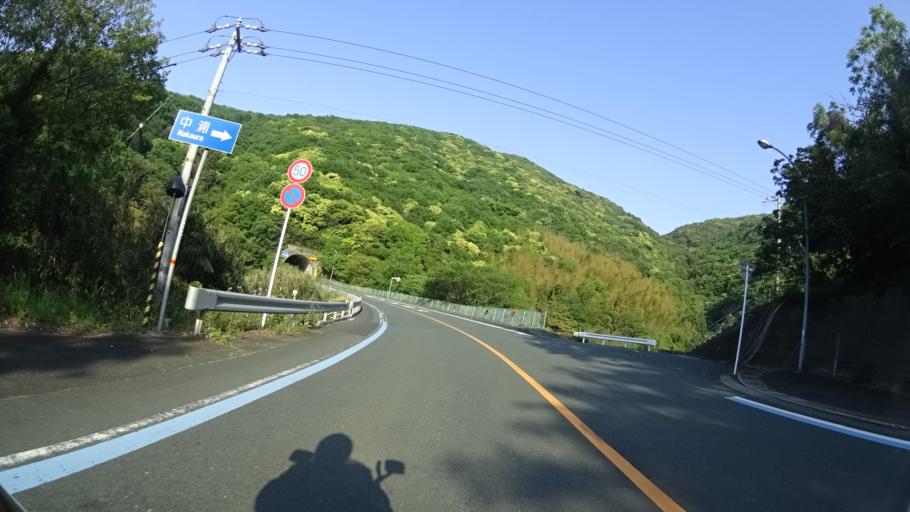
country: JP
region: Ehime
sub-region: Nishiuwa-gun
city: Ikata-cho
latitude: 33.4906
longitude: 132.3444
